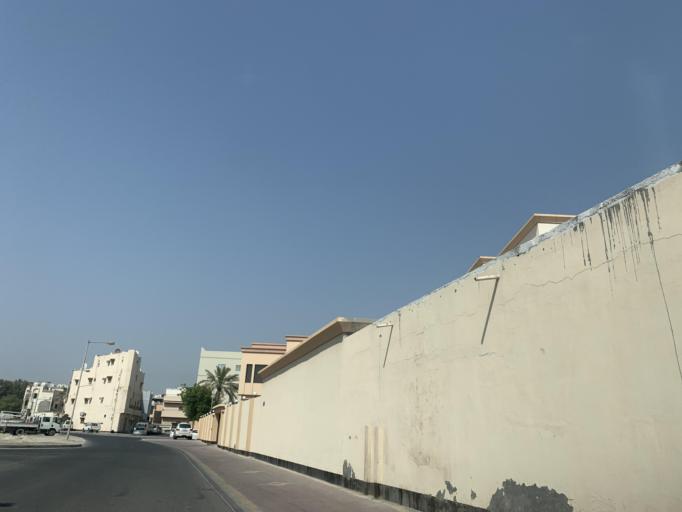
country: BH
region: Manama
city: Jidd Hafs
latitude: 26.2049
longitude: 50.5290
